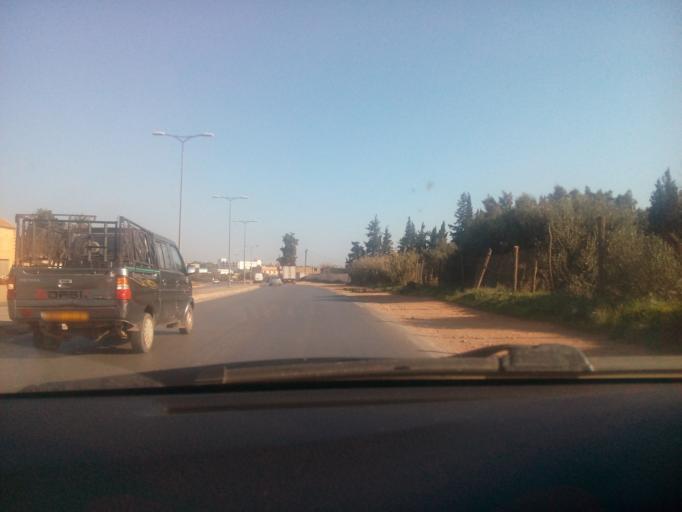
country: DZ
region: Oran
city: Oran
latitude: 35.6528
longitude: -0.6998
